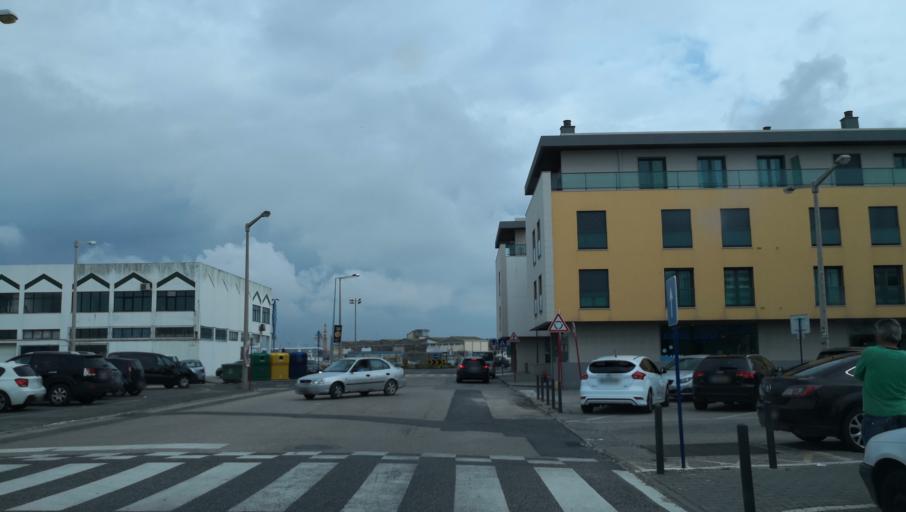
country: PT
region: Leiria
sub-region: Peniche
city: Peniche
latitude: 39.3588
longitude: -9.3738
